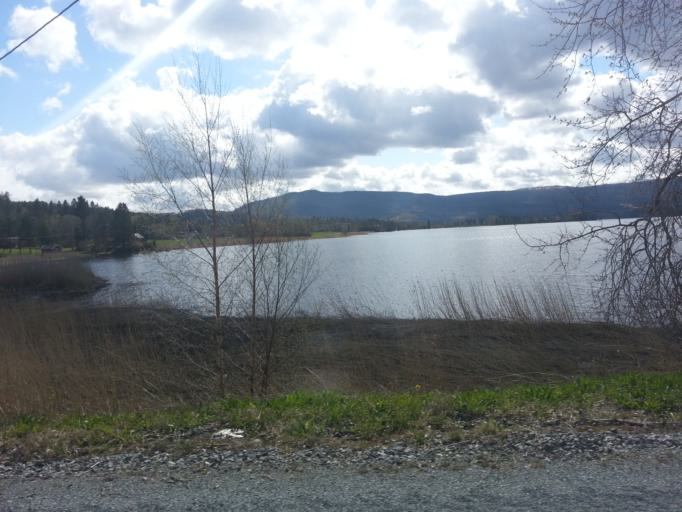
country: NO
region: Nord-Trondelag
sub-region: Levanger
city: Skogn
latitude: 63.6386
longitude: 11.2411
